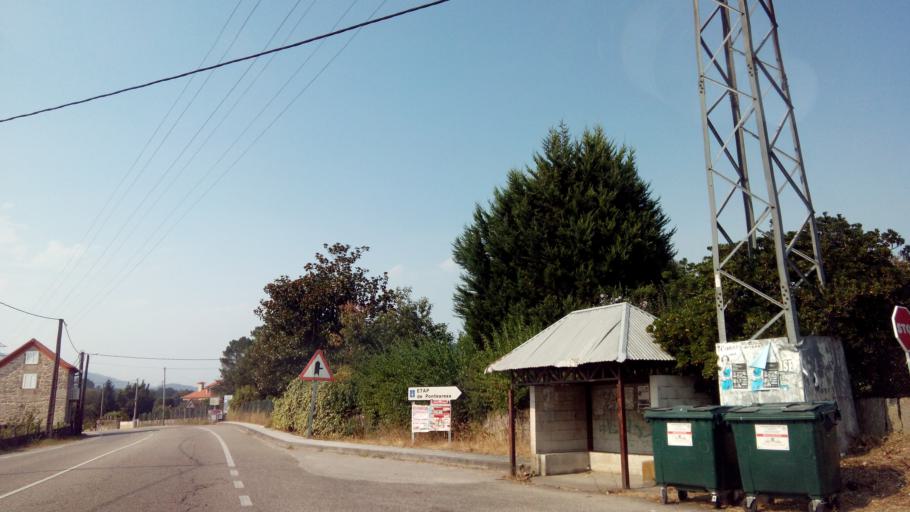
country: ES
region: Galicia
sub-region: Provincia de Pontevedra
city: Ponteareas
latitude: 42.1872
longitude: -8.5074
